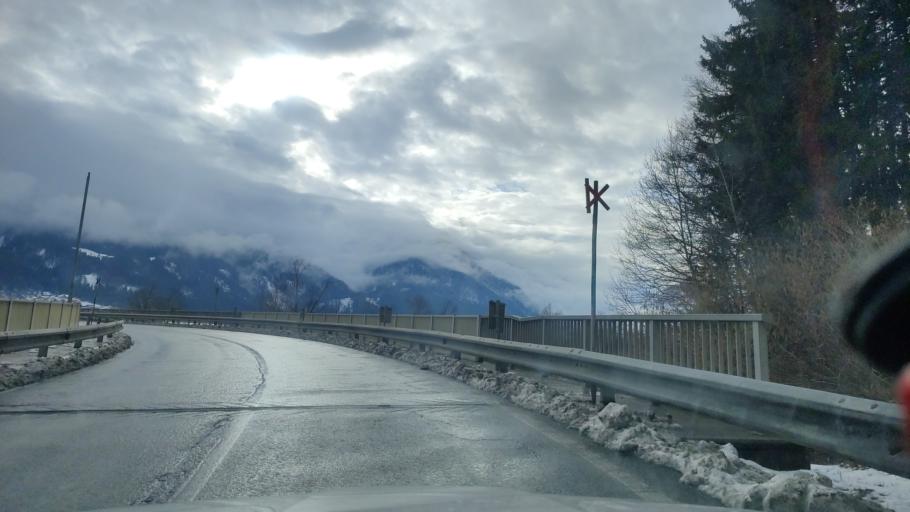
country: AT
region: Carinthia
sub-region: Politischer Bezirk Hermagor
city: Hermagor
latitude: 46.6236
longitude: 13.2885
